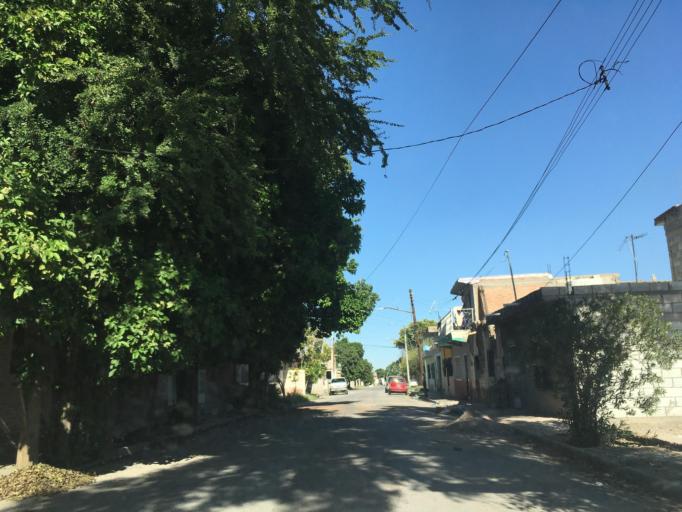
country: MX
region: Durango
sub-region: Lerdo
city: El Huarache (El Guarache)
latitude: 25.5428
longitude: -103.4741
